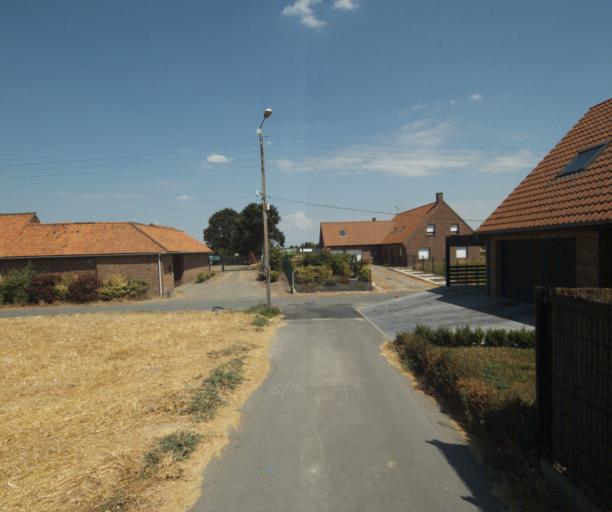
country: FR
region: Nord-Pas-de-Calais
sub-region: Departement du Nord
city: Neuville-en-Ferrain
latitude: 50.7523
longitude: 3.1768
